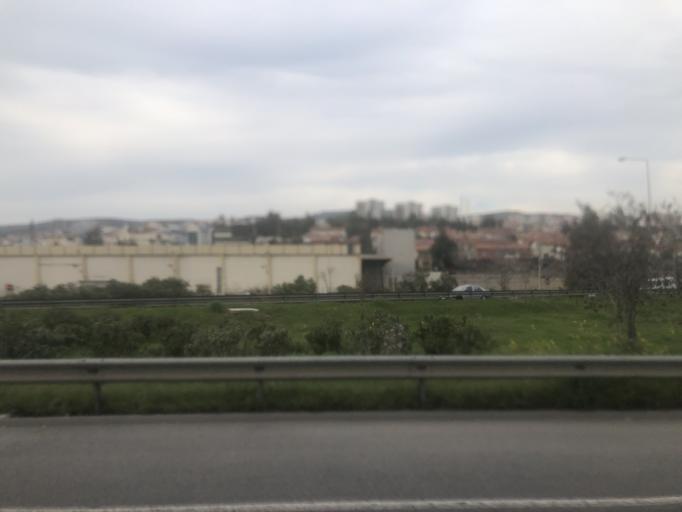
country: TR
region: Izmir
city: Karsiyaka
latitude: 38.4860
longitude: 27.0793
